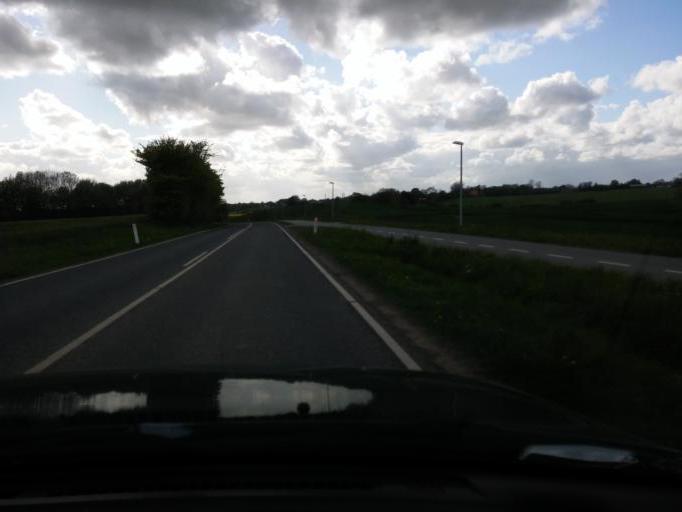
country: DK
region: South Denmark
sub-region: Faaborg-Midtfyn Kommune
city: Ringe
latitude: 55.2454
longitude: 10.5162
